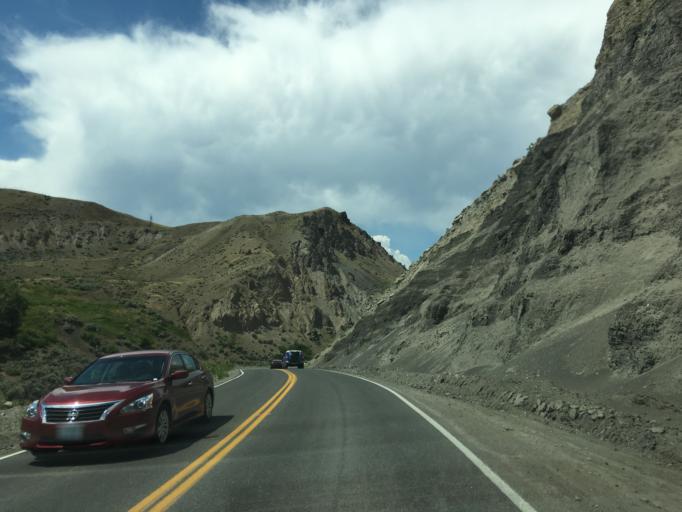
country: US
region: Montana
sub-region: Gallatin County
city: West Yellowstone
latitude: 45.0071
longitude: -110.6936
